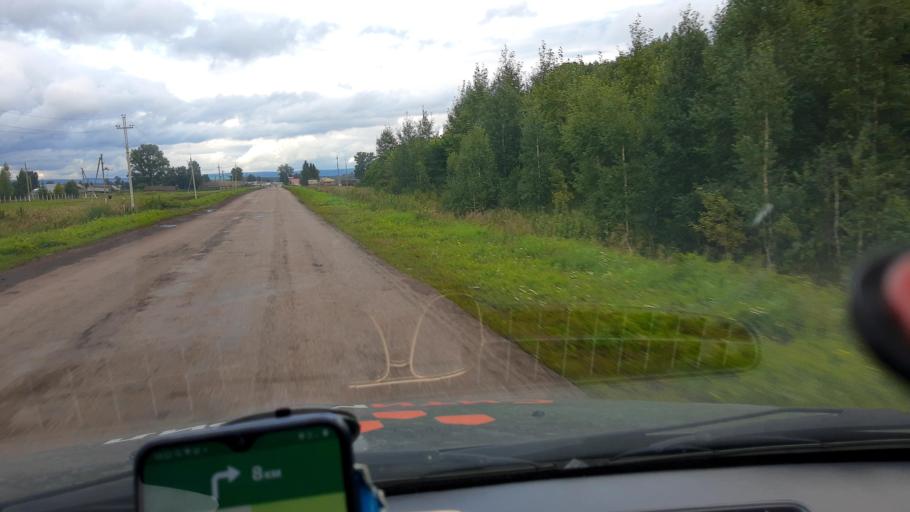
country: RU
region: Bashkortostan
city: Tolbazy
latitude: 53.9888
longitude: 56.2681
